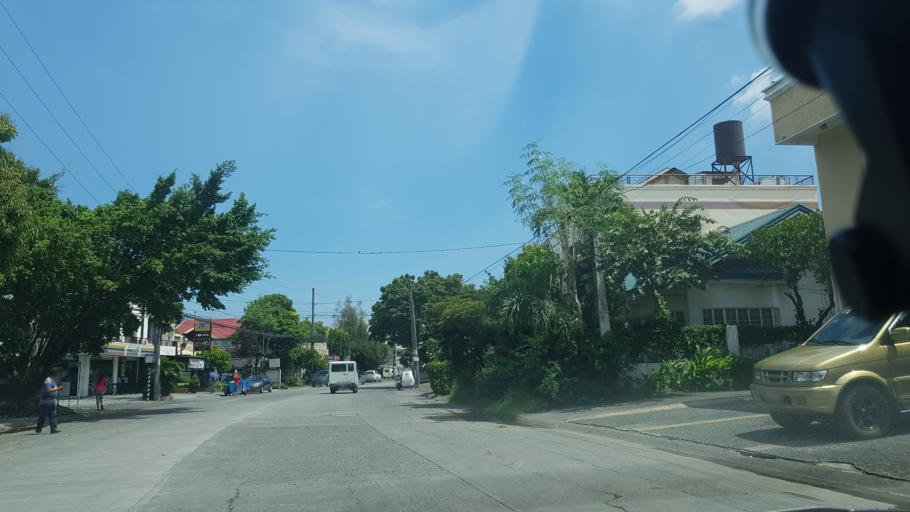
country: PH
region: Calabarzon
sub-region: Province of Rizal
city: Las Pinas
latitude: 14.4358
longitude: 120.9893
